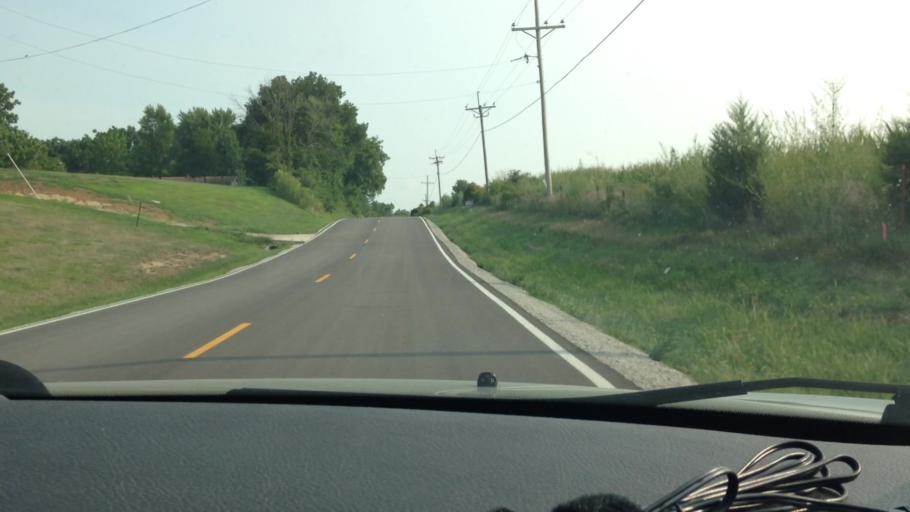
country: US
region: Missouri
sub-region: Platte County
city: Platte City
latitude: 39.3919
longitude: -94.7796
